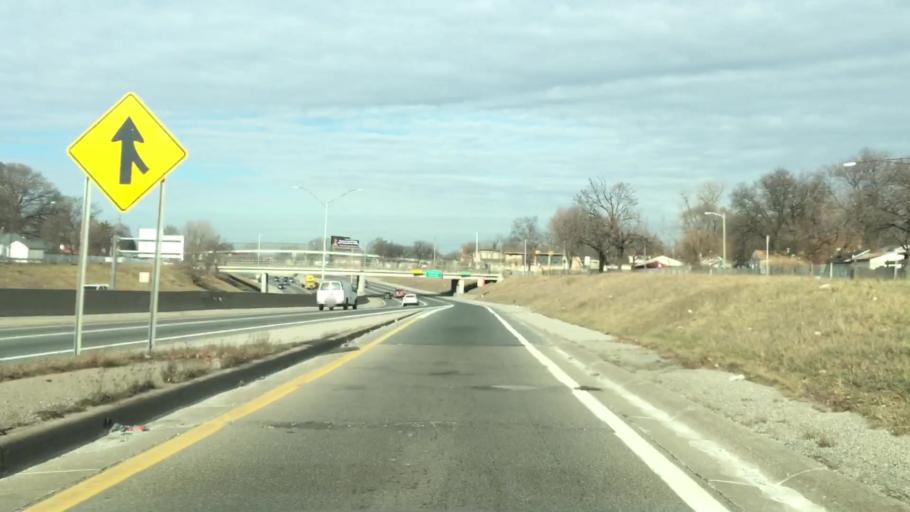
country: US
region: Michigan
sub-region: Oakland County
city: Hazel Park
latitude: 42.4530
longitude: -83.0948
